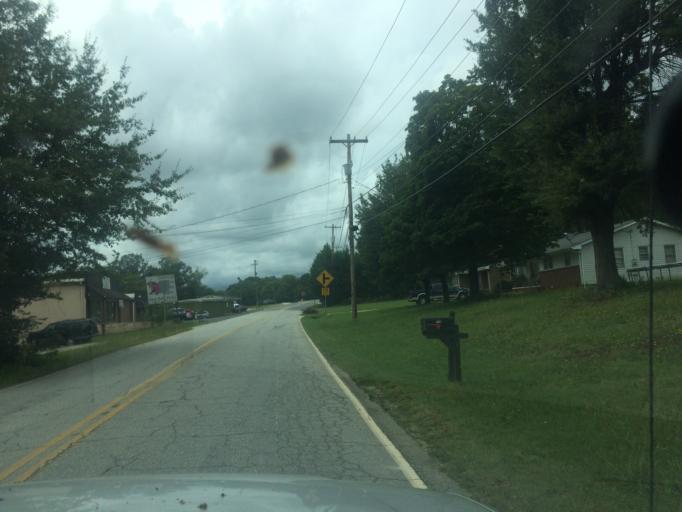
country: US
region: South Carolina
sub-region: Greenville County
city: Greer
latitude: 34.9452
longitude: -82.2588
